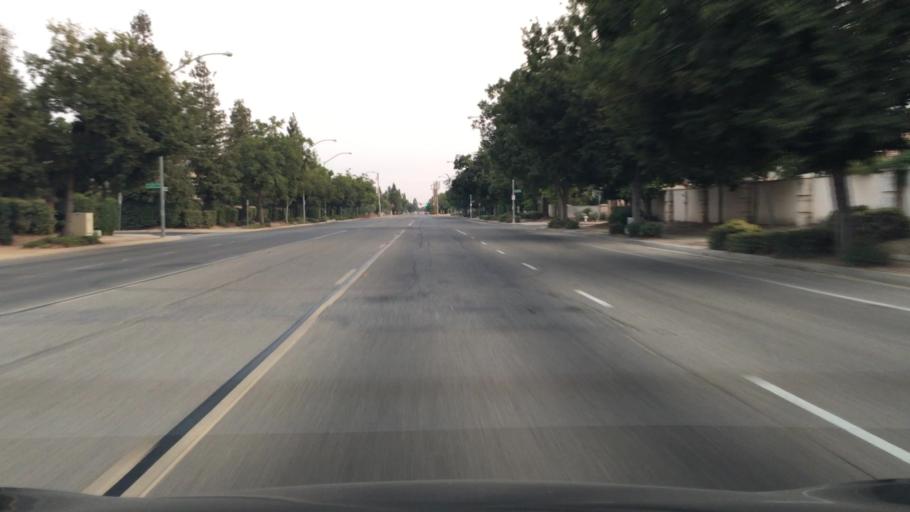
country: US
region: California
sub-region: Fresno County
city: Clovis
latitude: 36.8649
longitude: -119.7478
